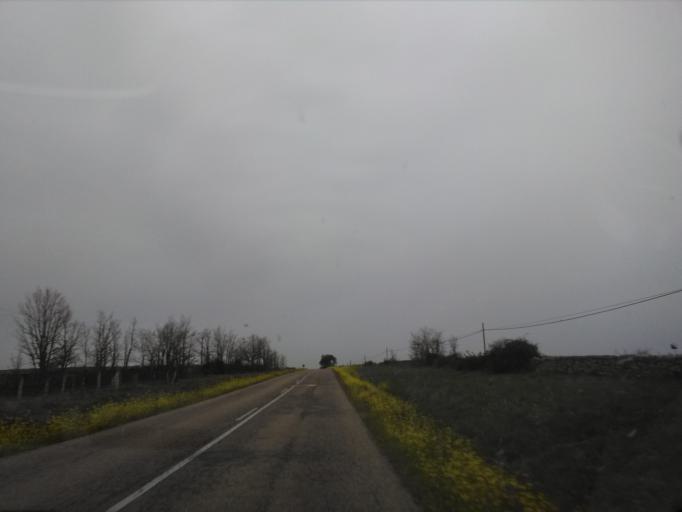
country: ES
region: Castille and Leon
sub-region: Provincia de Salamanca
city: Moronta
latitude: 40.9827
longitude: -6.4642
